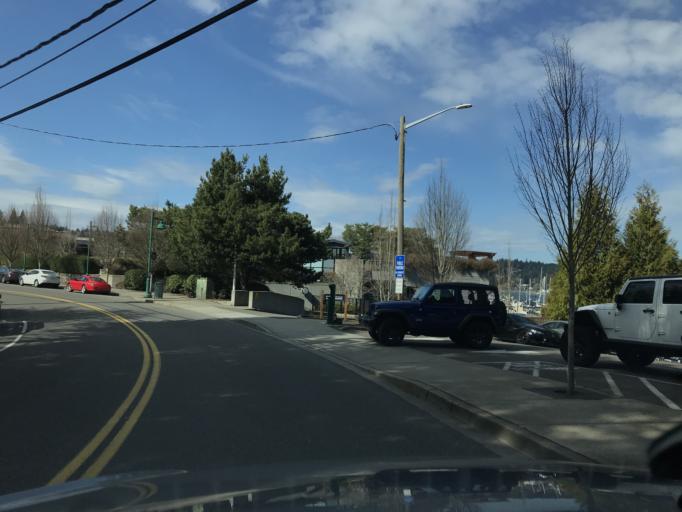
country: US
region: Washington
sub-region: Pierce County
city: Gig Harbor
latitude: 47.3291
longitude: -122.5789
